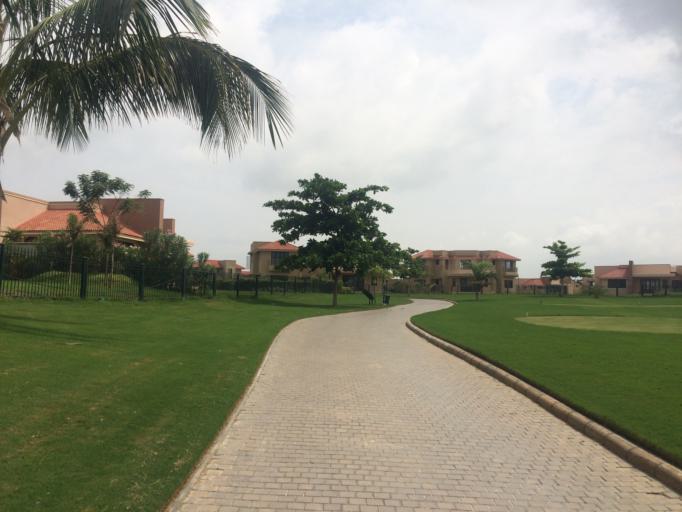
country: IN
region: Gujarat
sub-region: Ahmadabad
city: Sanand
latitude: 23.0212
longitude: 72.3601
